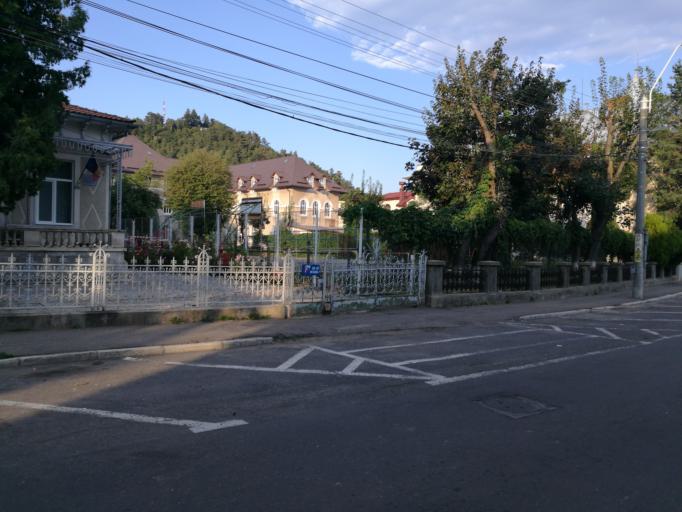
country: RO
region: Neamt
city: Piatra Neamt
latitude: 46.9335
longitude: 26.3645
